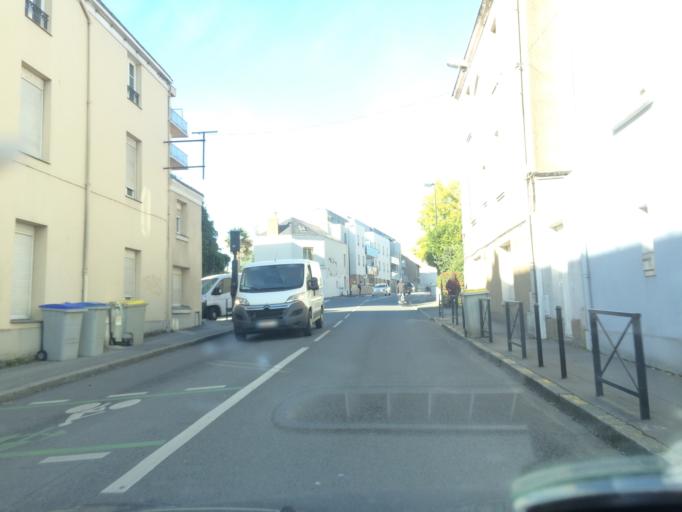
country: FR
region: Pays de la Loire
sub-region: Departement de la Loire-Atlantique
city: Nantes
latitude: 47.2349
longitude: -1.5413
